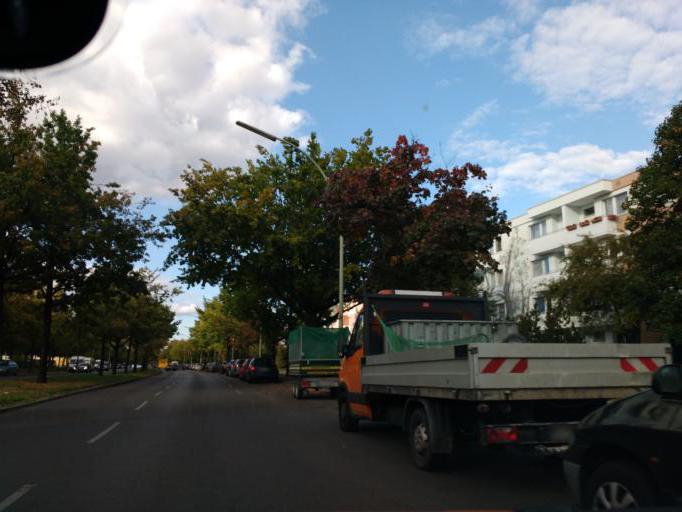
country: DE
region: Berlin
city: Britz
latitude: 52.4326
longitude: 13.4353
